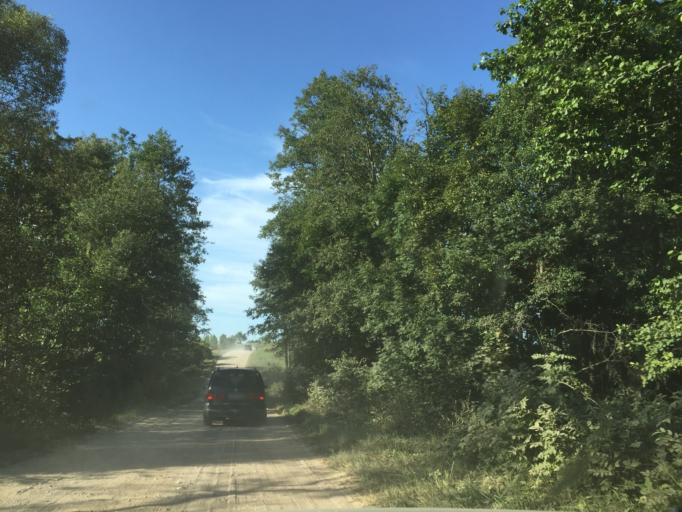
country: LT
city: Zarasai
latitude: 55.7946
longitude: 25.9524
